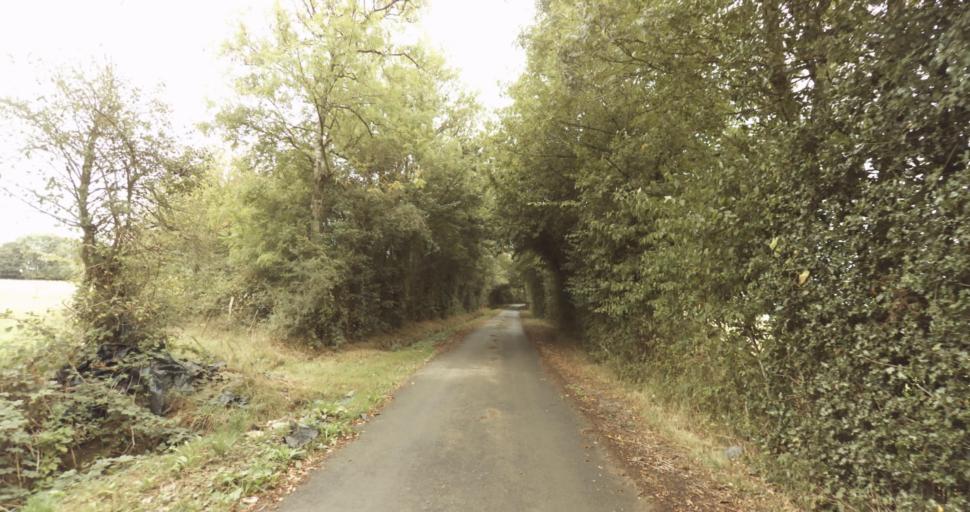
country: FR
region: Lower Normandy
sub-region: Departement de l'Orne
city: Sainte-Gauburge-Sainte-Colombe
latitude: 48.7129
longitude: 0.4495
